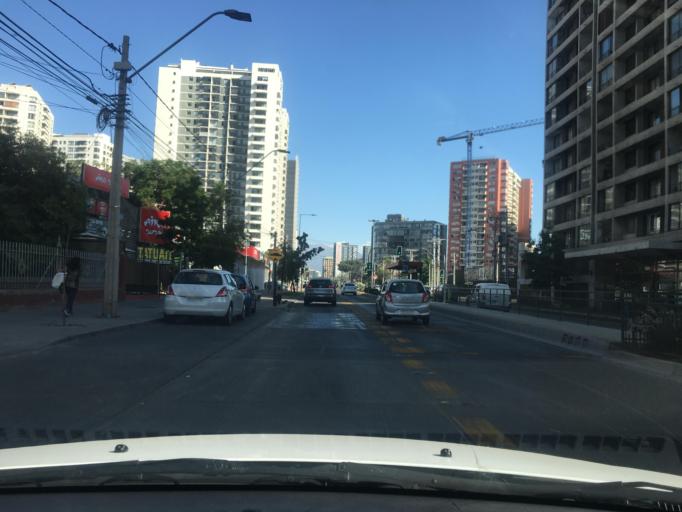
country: CL
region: Santiago Metropolitan
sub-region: Provincia de Santiago
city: Villa Presidente Frei, Nunoa, Santiago, Chile
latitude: -33.5151
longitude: -70.6072
